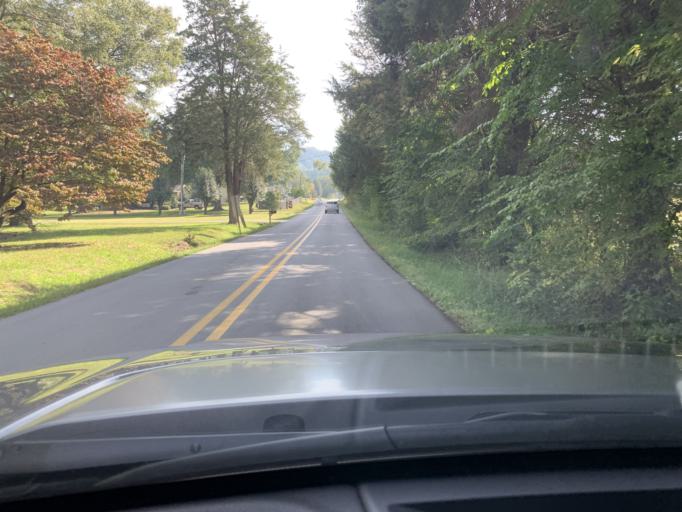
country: US
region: Georgia
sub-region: Polk County
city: Aragon
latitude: 34.0356
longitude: -85.0392
